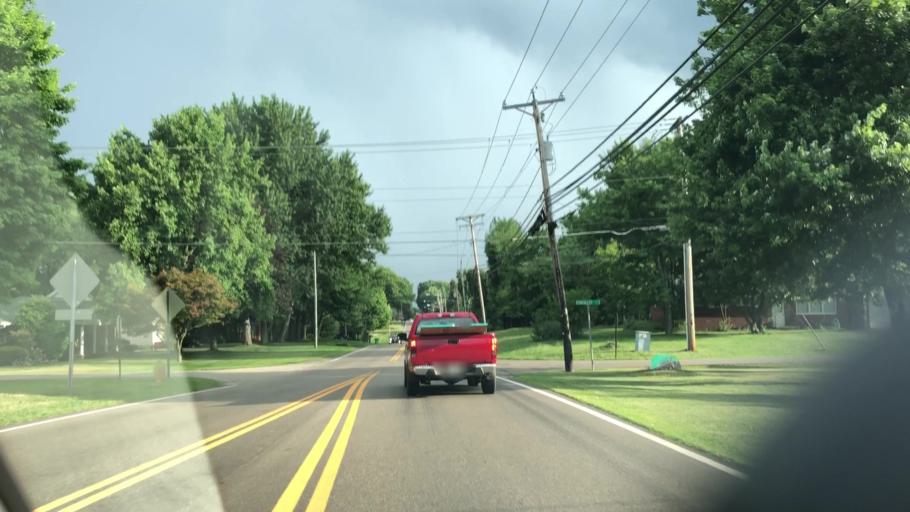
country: US
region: Ohio
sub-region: Stark County
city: North Canton
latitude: 40.8627
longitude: -81.4422
